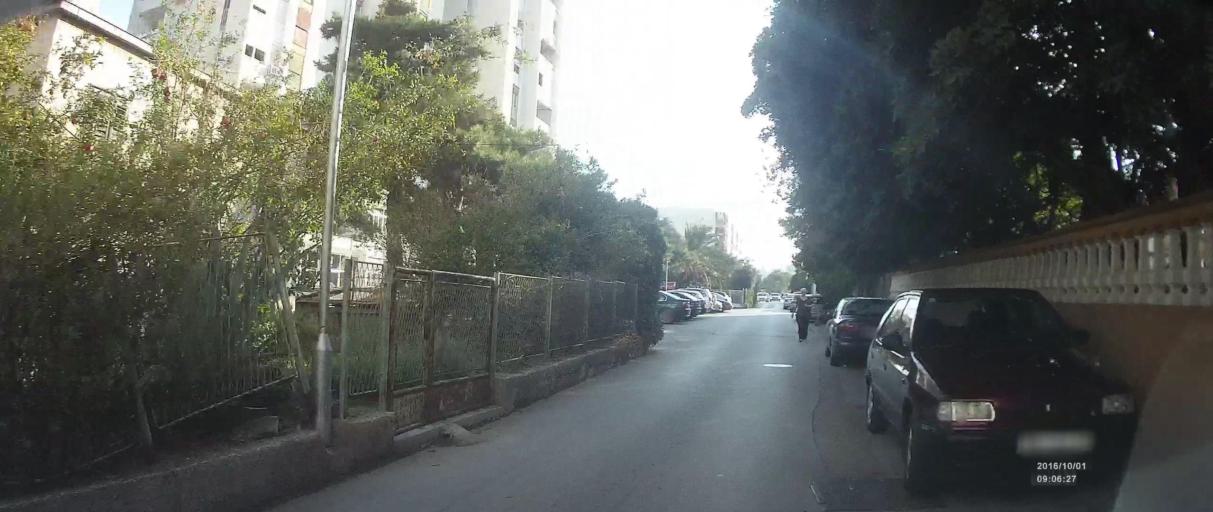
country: HR
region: Splitsko-Dalmatinska
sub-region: Grad Split
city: Split
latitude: 43.5192
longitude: 16.4515
